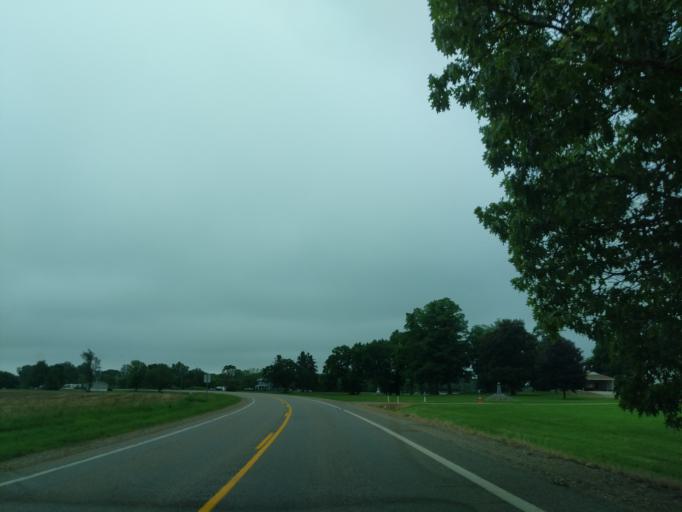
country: US
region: Michigan
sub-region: Hillsdale County
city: Litchfield
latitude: 42.0775
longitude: -84.8026
